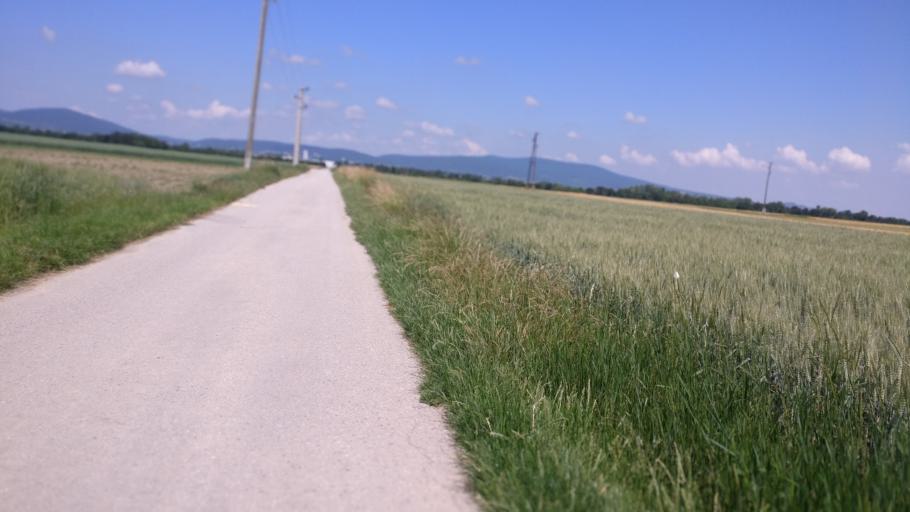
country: AT
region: Lower Austria
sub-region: Politischer Bezirk Baden
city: Teesdorf
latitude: 47.9549
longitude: 16.2884
